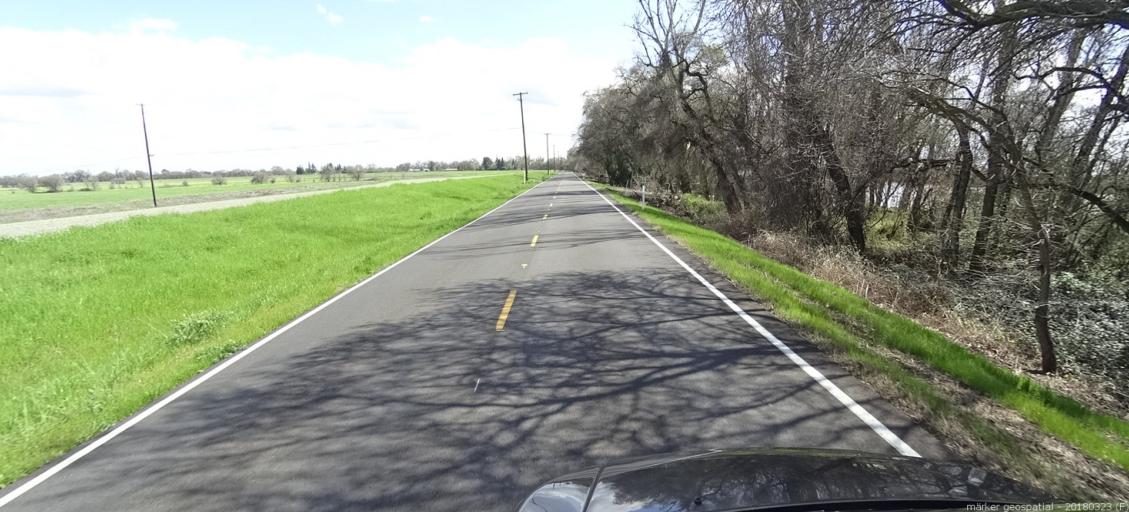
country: US
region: California
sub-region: Yolo County
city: West Sacramento
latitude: 38.6504
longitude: -121.5978
